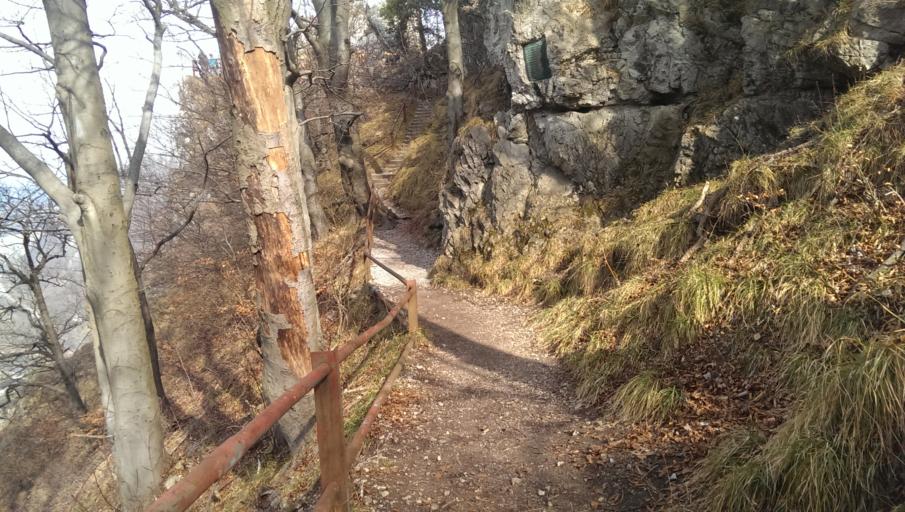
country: AT
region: Styria
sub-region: Graz Stadt
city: Goesting
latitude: 47.1044
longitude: 15.3828
